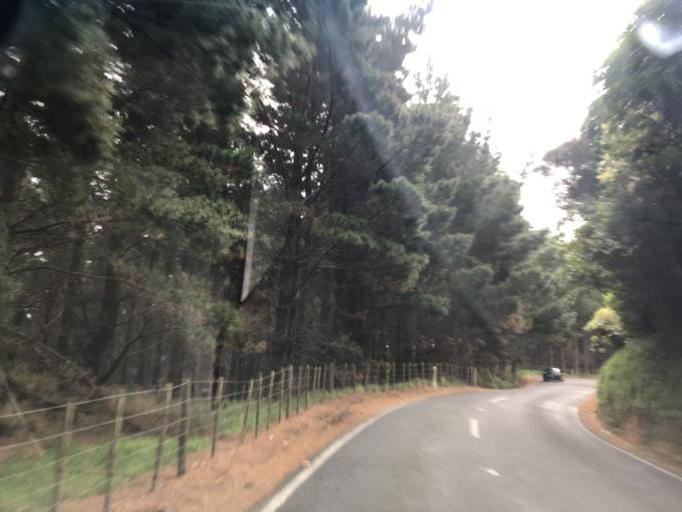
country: NZ
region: Wellington
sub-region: Wellington City
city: Kelburn
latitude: -41.2122
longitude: 174.7939
